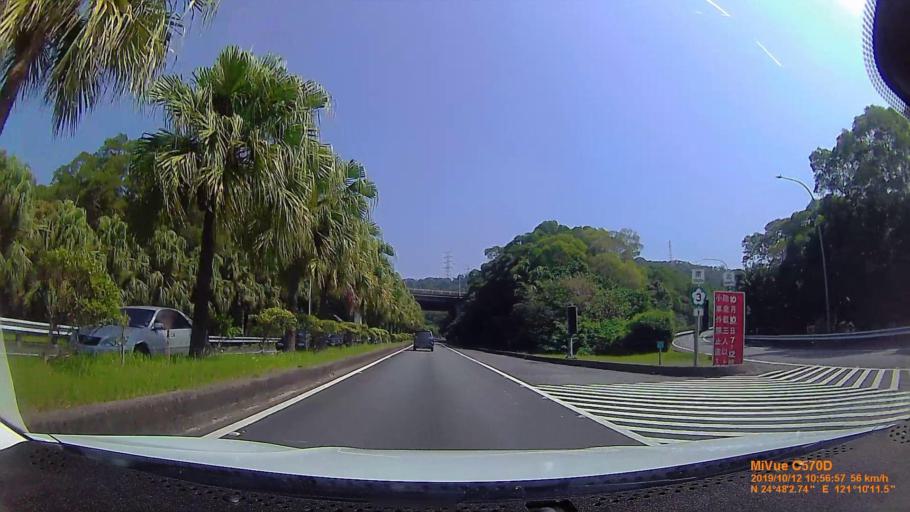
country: TW
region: Taiwan
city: Daxi
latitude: 24.8008
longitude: 121.1699
